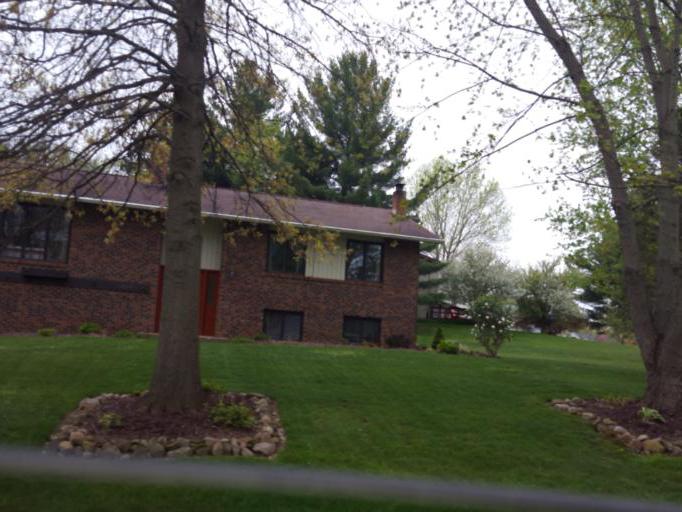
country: US
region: Ohio
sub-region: Richland County
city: Lexington
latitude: 40.7085
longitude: -82.6090
